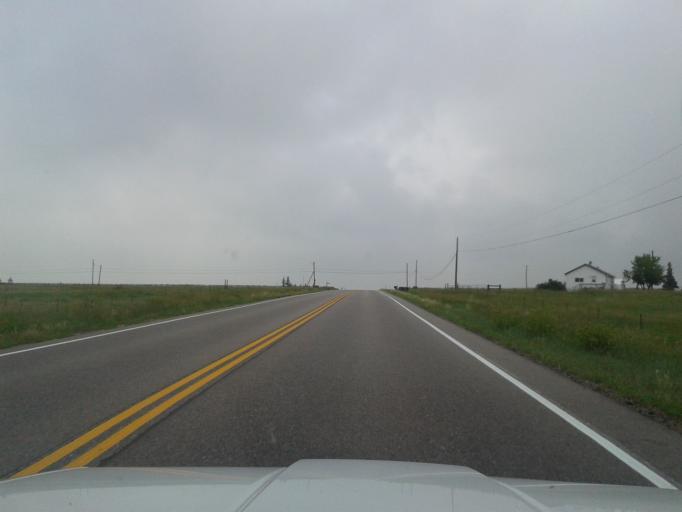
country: US
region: Colorado
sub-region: Elbert County
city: Ponderosa Park
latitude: 39.3387
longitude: -104.7339
